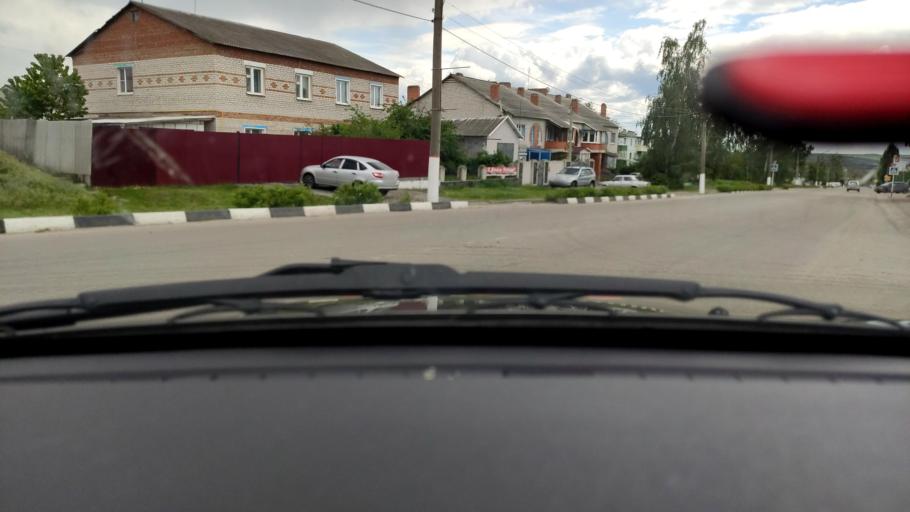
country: RU
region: Voronezj
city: Rossosh'
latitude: 51.0857
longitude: 38.6442
